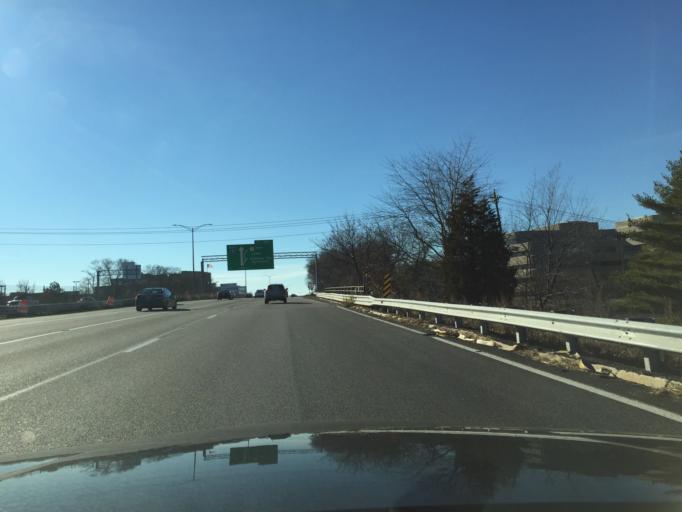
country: US
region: Massachusetts
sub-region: Middlesex County
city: Burlington
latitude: 42.4859
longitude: -71.1959
